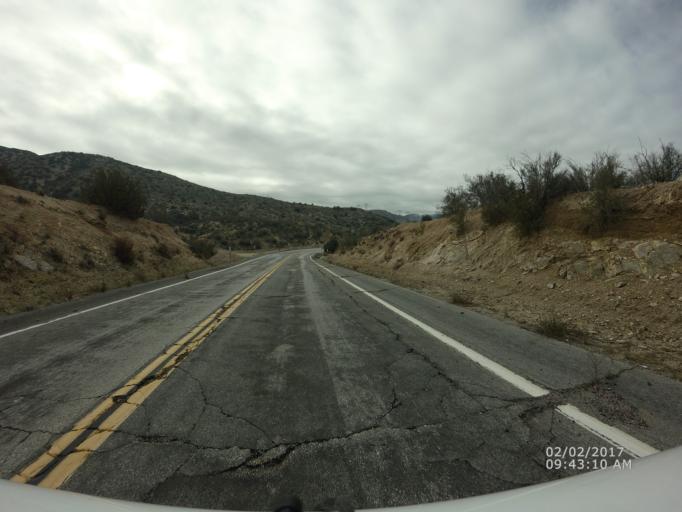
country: US
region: California
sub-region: Los Angeles County
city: Vincent
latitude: 34.4502
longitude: -118.0985
